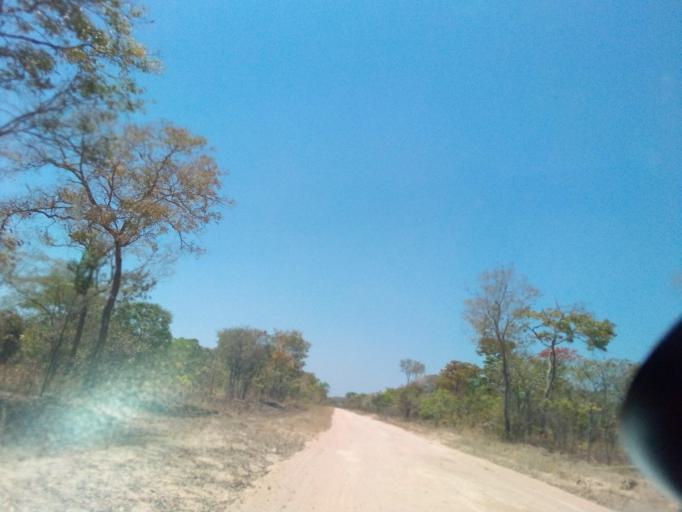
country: ZM
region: Northern
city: Mpika
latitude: -12.2400
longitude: 30.6616
